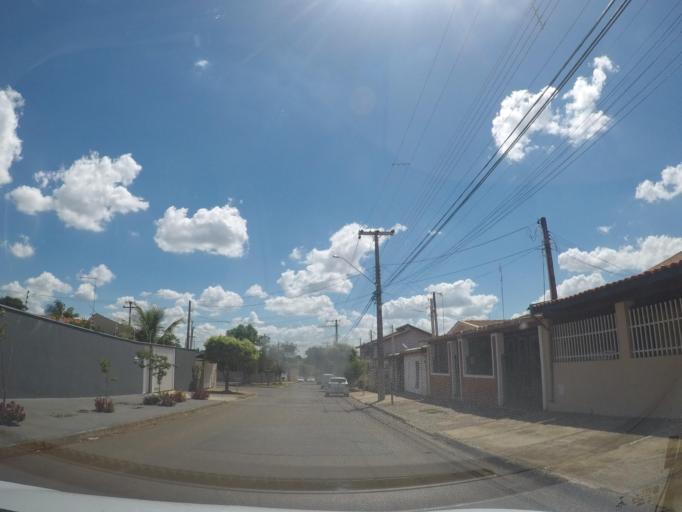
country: BR
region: Sao Paulo
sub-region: Sumare
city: Sumare
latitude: -22.8326
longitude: -47.2755
